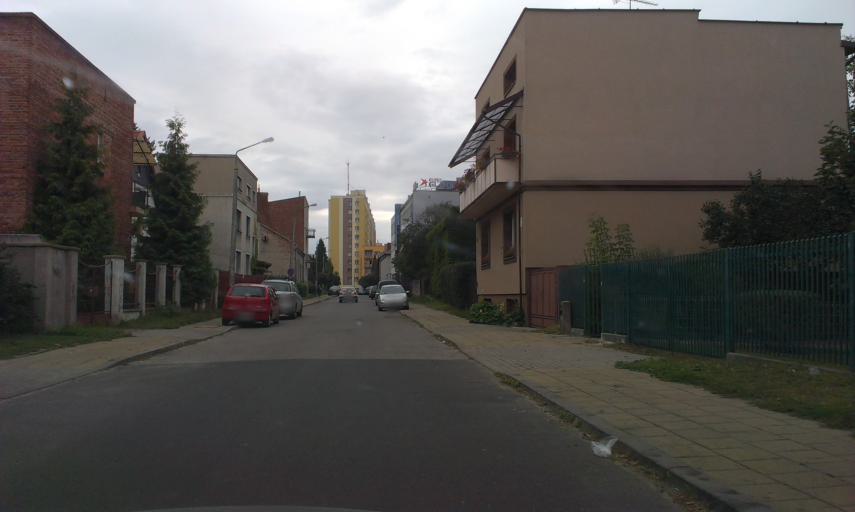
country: PL
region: Masovian Voivodeship
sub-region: Radom
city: Radom
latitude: 51.4038
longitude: 21.1633
